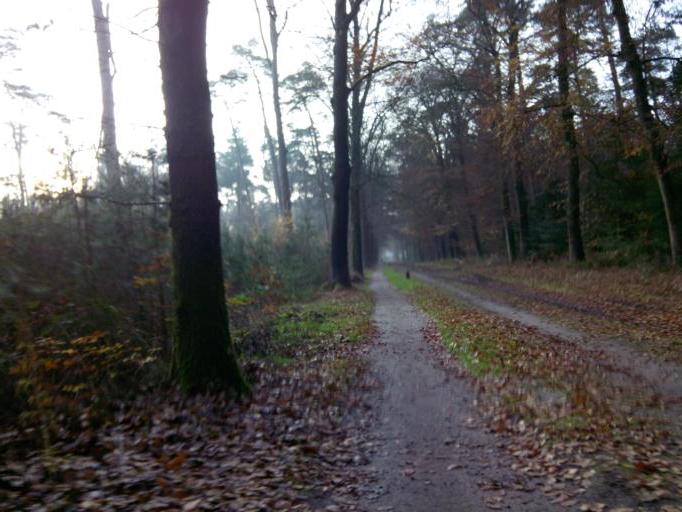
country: NL
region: Utrecht
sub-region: Gemeente Woudenberg
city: Woudenberg
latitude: 52.1097
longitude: 5.3891
